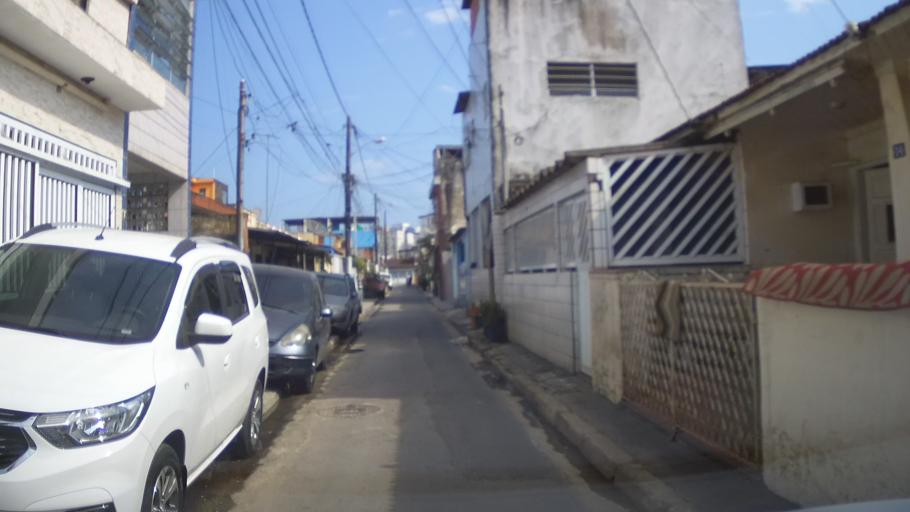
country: BR
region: Sao Paulo
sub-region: Santos
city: Santos
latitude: -23.9626
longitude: -46.3075
